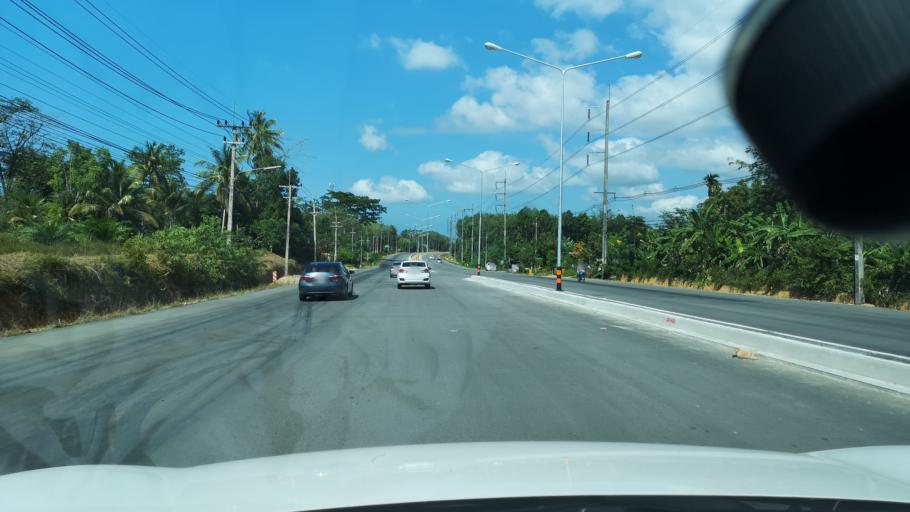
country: TH
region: Phangnga
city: Thai Mueang
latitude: 8.4333
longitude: 98.2576
